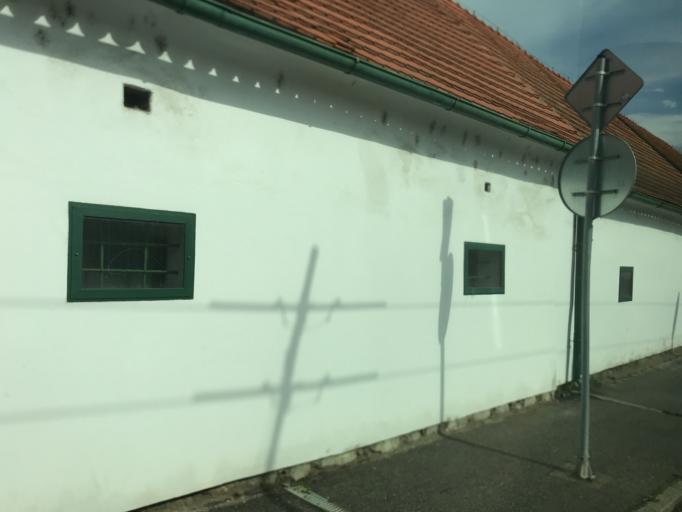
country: CZ
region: Jihocesky
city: Litvinovice
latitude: 48.9482
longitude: 14.4649
